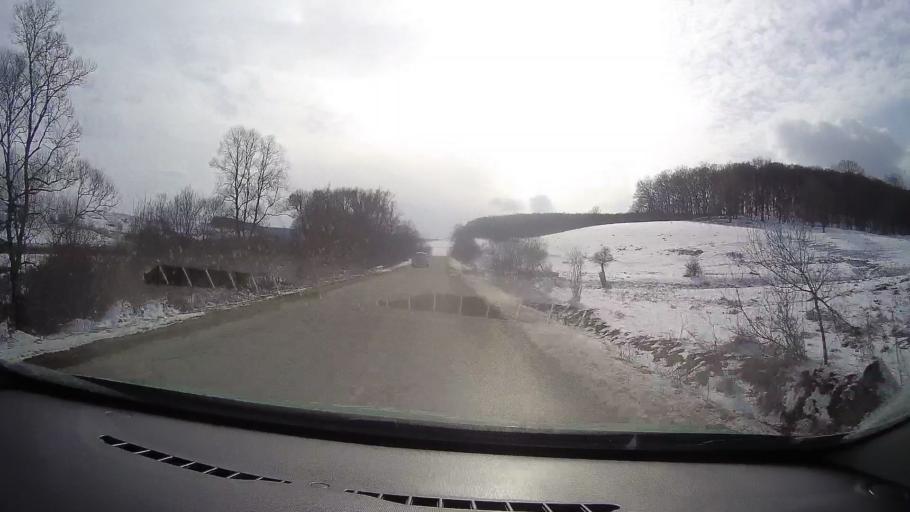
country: RO
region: Sibiu
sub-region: Comuna Bradeni
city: Bradeni
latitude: 46.0950
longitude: 24.8359
